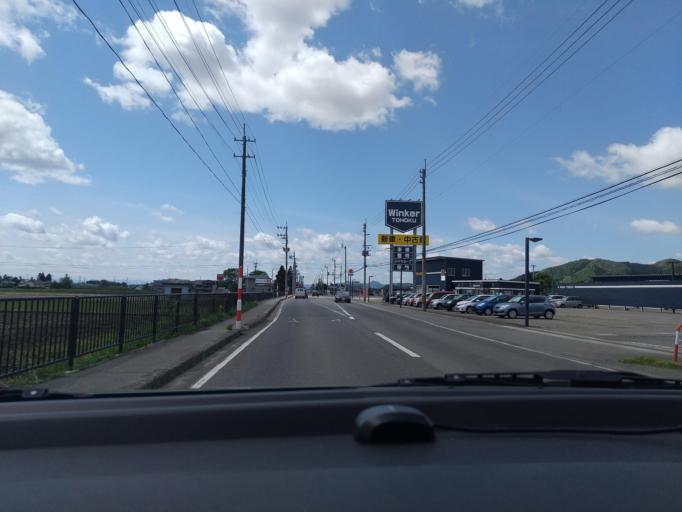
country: JP
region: Akita
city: Kakunodatemachi
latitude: 39.5583
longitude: 140.5557
